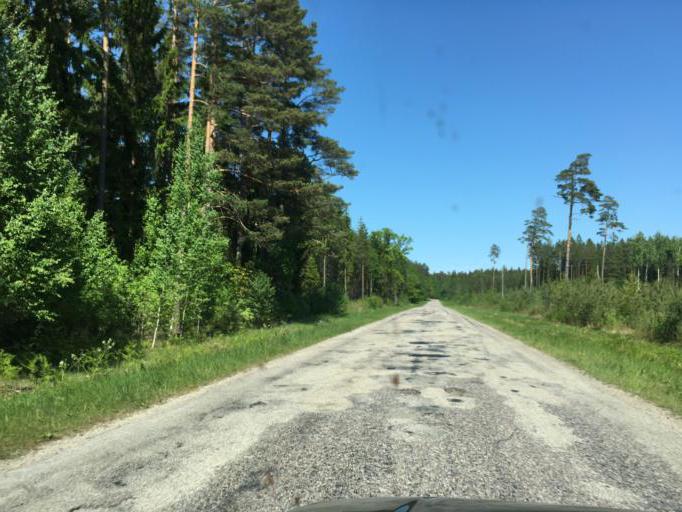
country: LV
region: Dundaga
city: Dundaga
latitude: 57.4791
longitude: 22.3309
